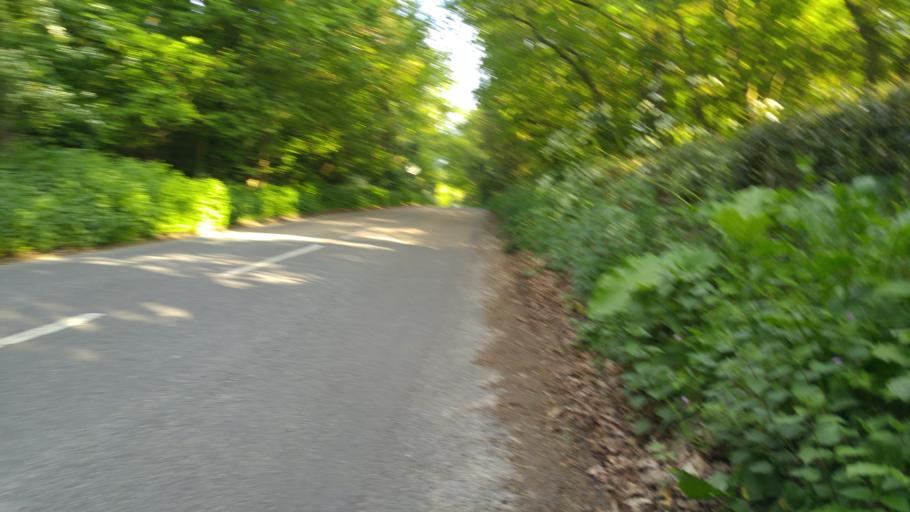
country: GB
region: England
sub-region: Essex
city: Tiptree
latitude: 51.8318
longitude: 0.7476
